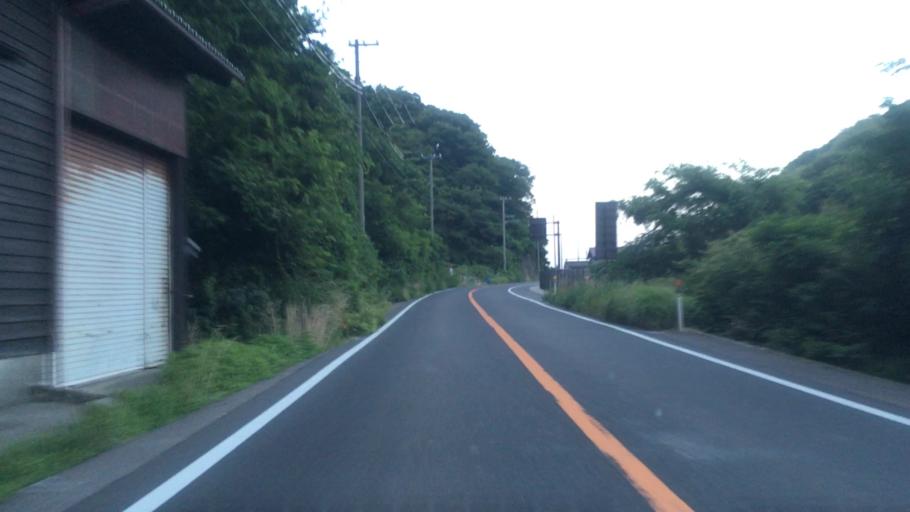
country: JP
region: Tottori
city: Tottori
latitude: 35.6162
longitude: 134.3946
